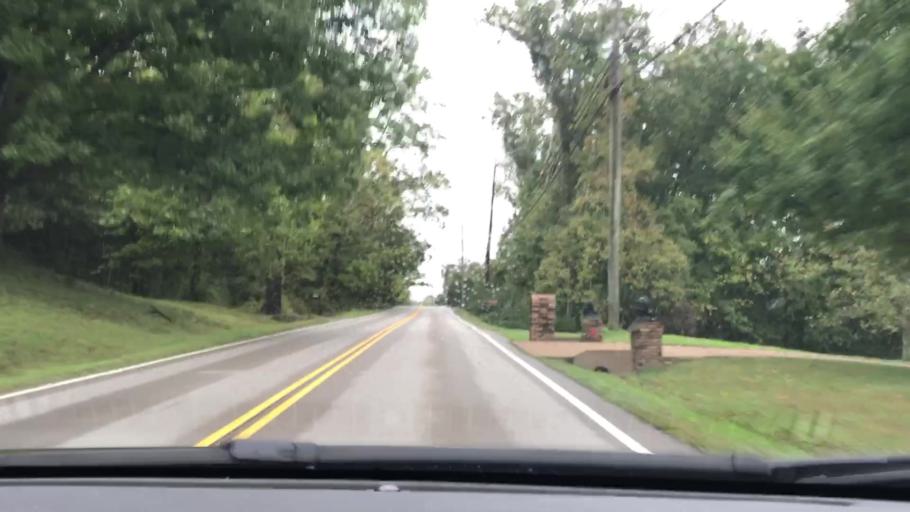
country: US
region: Tennessee
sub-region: Williamson County
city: Brentwood Estates
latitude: 36.0144
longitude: -86.7232
